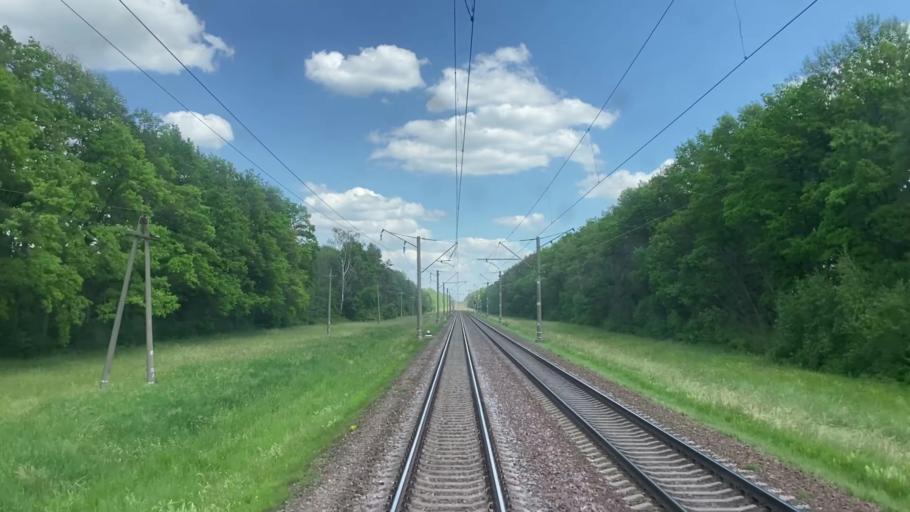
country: BY
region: Brest
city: Pruzhany
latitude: 52.4886
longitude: 24.5811
